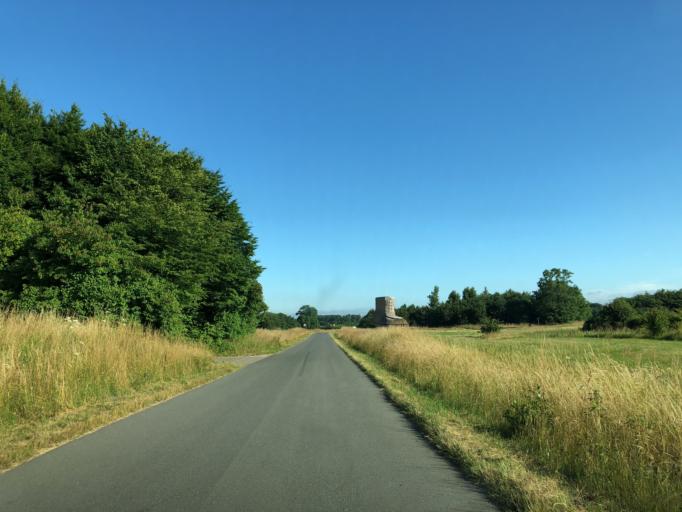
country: DK
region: South Denmark
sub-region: Sonderborg Kommune
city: Sonderborg
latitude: 54.9308
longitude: 9.7745
